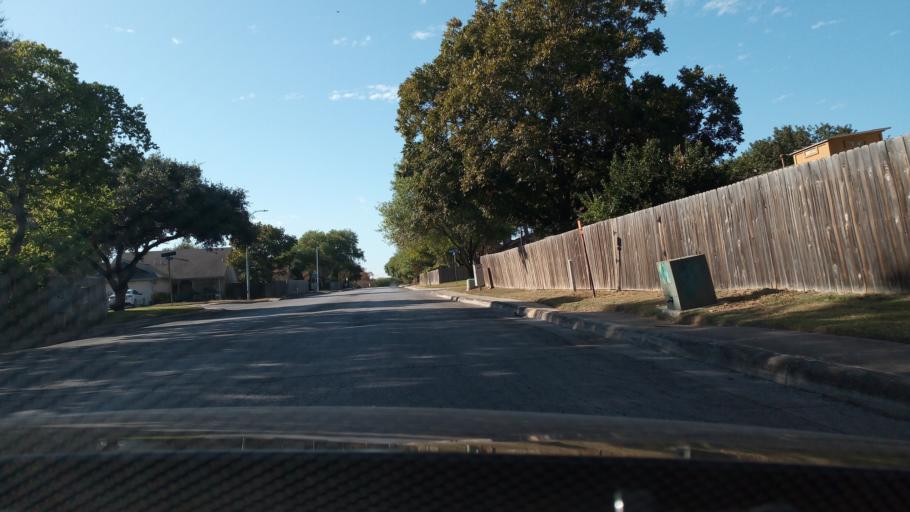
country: US
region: Texas
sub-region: Bexar County
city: Windcrest
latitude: 29.5564
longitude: -98.4335
